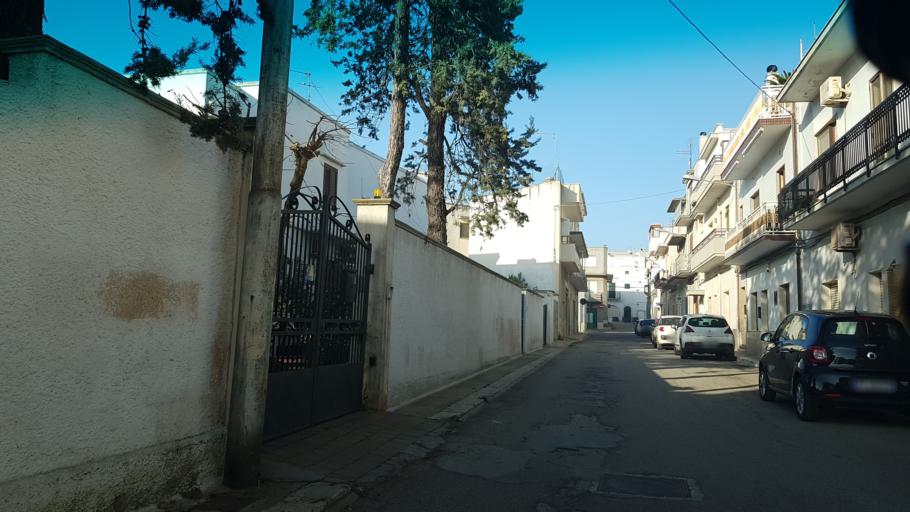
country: IT
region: Apulia
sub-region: Provincia di Brindisi
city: Carovigno
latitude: 40.7031
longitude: 17.6547
